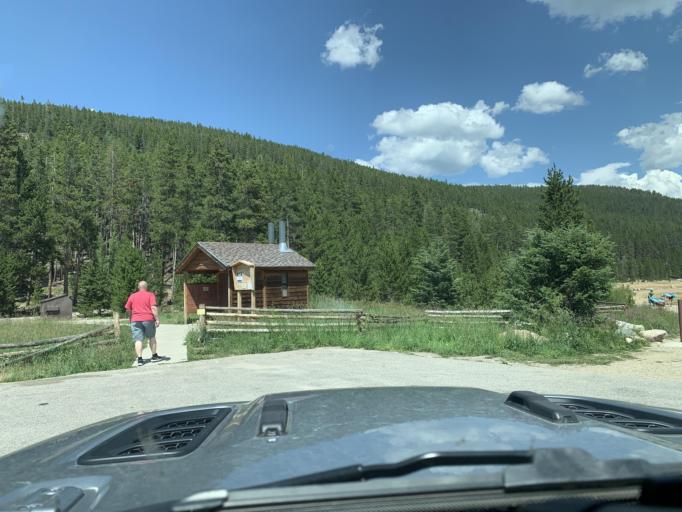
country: US
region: Colorado
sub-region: Lake County
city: Leadville North
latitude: 39.2774
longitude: -106.4312
